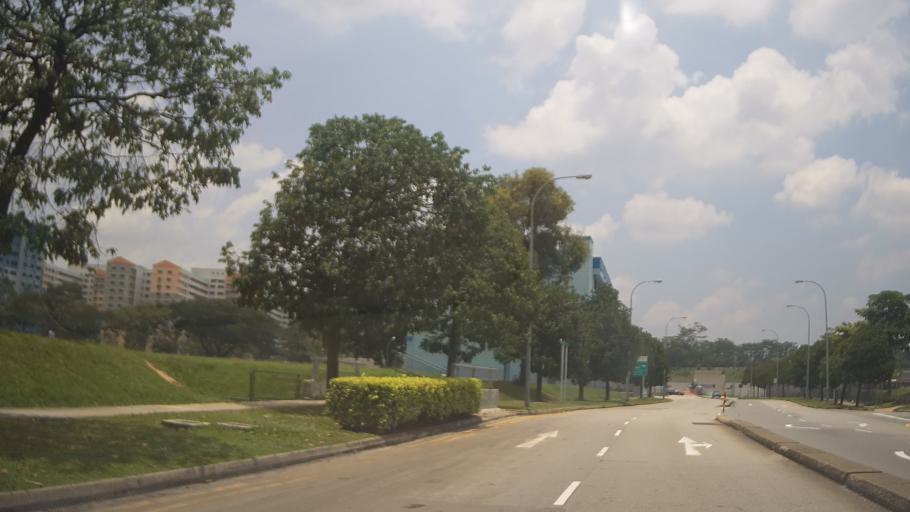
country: MY
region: Johor
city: Johor Bahru
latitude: 1.4479
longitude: 103.7940
